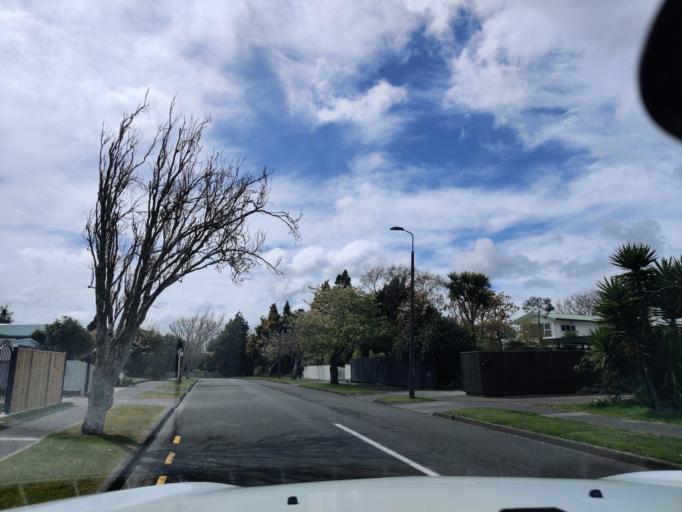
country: NZ
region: Manawatu-Wanganui
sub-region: Palmerston North City
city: Palmerston North
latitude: -40.3795
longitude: 175.5972
